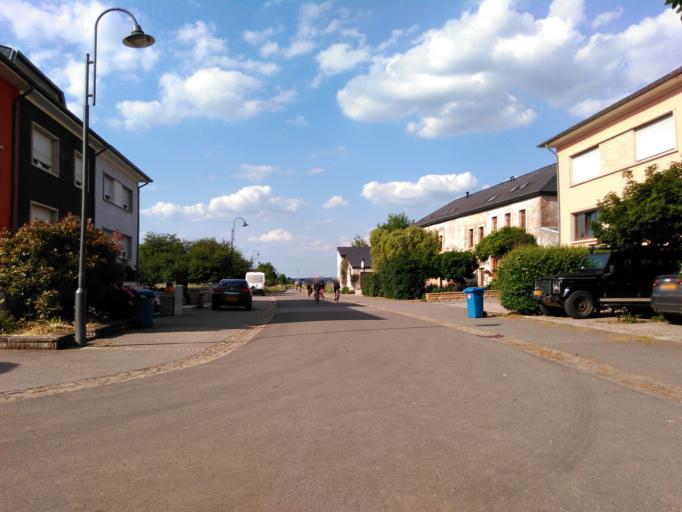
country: LU
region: Luxembourg
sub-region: Canton d'Esch-sur-Alzette
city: Kayl
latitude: 49.4908
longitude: 6.0414
